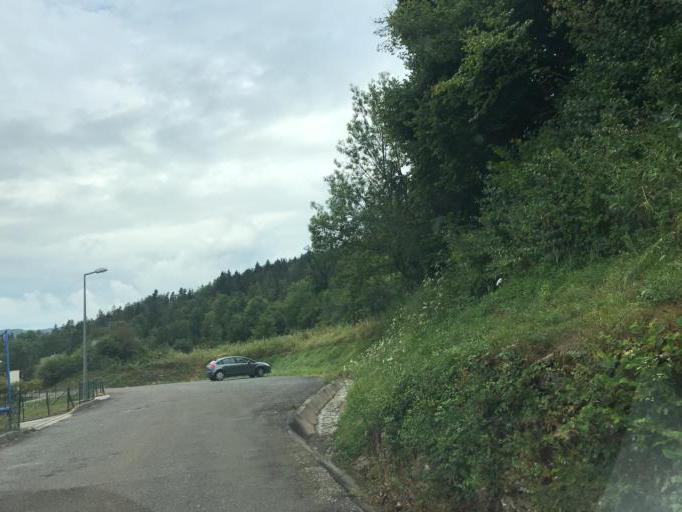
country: FR
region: Franche-Comte
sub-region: Departement du Jura
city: Lavans-les-Saint-Claude
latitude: 46.3625
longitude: 5.7883
